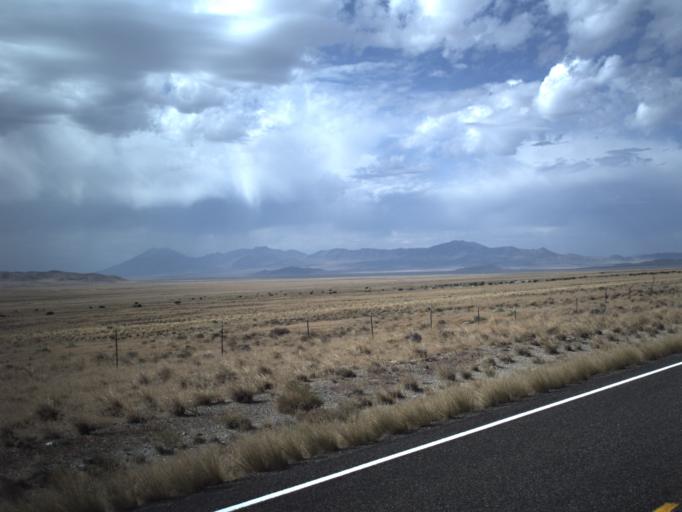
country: US
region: Utah
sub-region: Tooele County
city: Wendover
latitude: 41.4396
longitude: -113.7172
